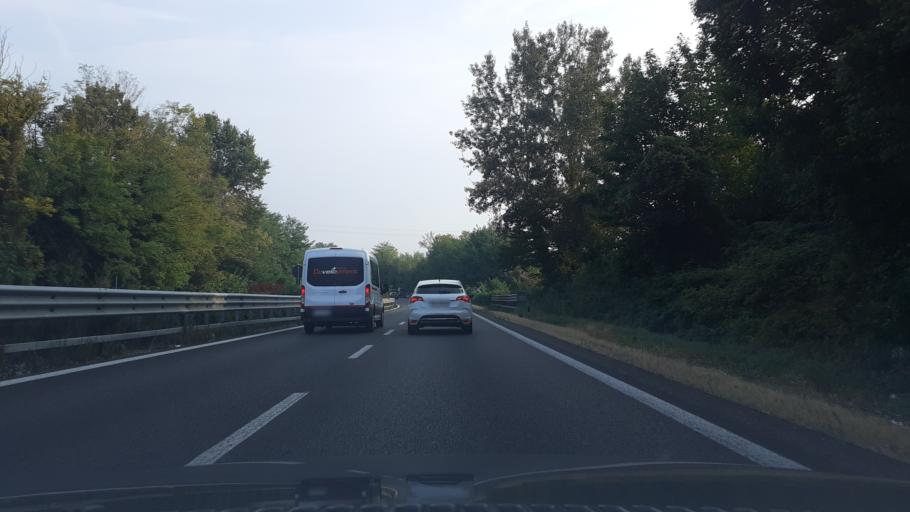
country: IT
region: Lombardy
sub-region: Provincia di Monza e Brianza
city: Verano Brianza
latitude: 45.7004
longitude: 9.2305
